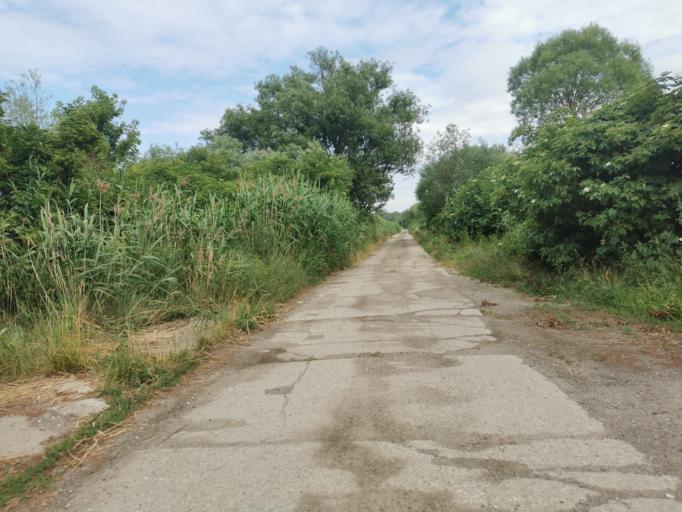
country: CZ
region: South Moravian
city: Tynec
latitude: 48.7638
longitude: 17.0616
